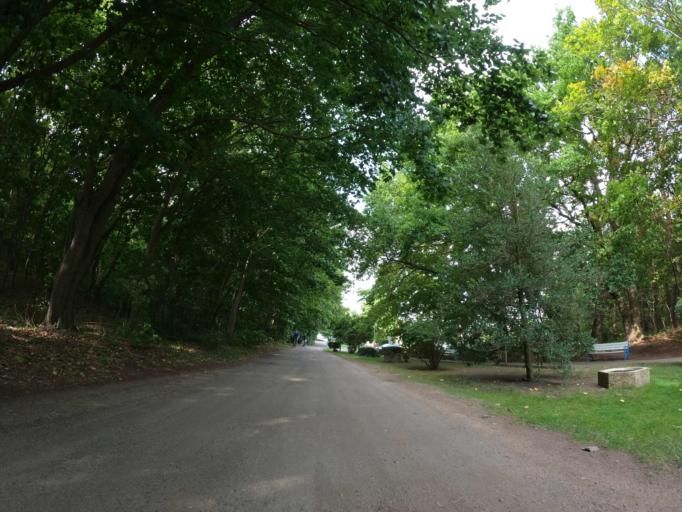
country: DE
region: Mecklenburg-Vorpommern
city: Ostseebad Gohren
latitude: 54.2760
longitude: 13.7213
